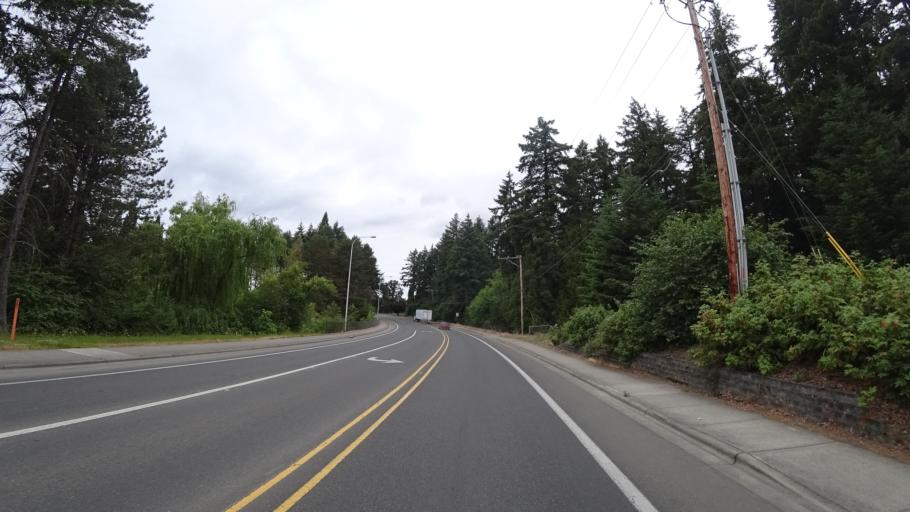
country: US
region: Oregon
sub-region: Washington County
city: Hillsboro
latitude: 45.4941
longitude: -122.9400
